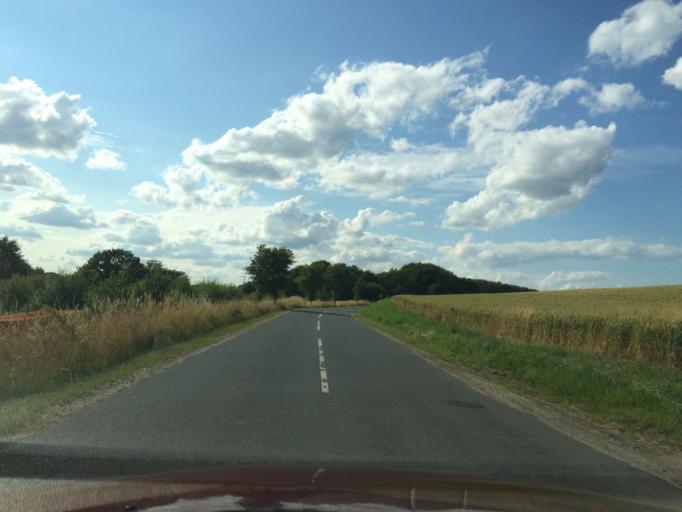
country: DK
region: Central Jutland
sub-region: Favrskov Kommune
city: Hammel
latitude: 56.2438
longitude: 9.7251
